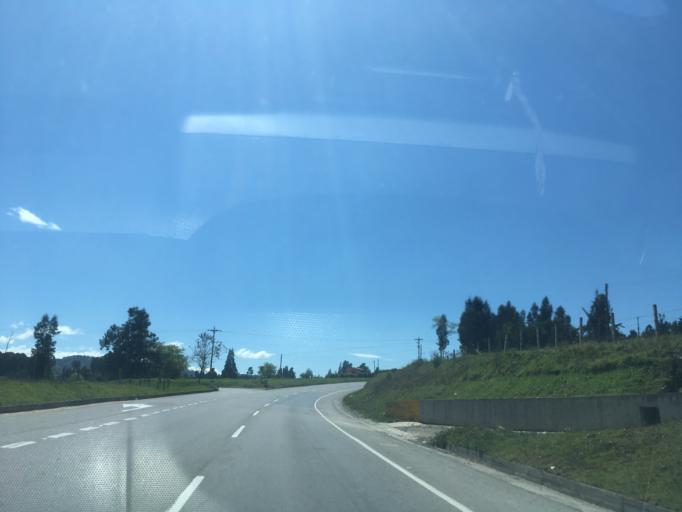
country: CO
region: Boyaca
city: Tuta
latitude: 5.7218
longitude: -73.2264
